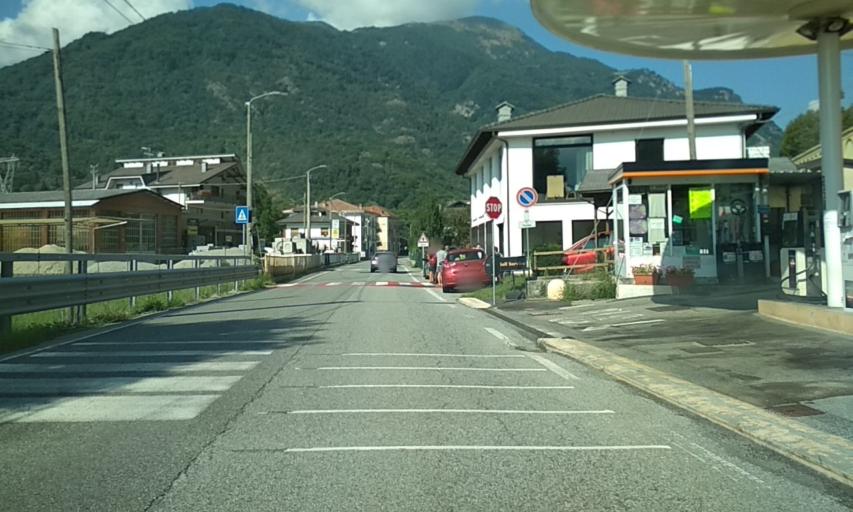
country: IT
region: Piedmont
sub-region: Provincia di Torino
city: Locana
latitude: 45.4164
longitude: 7.4641
